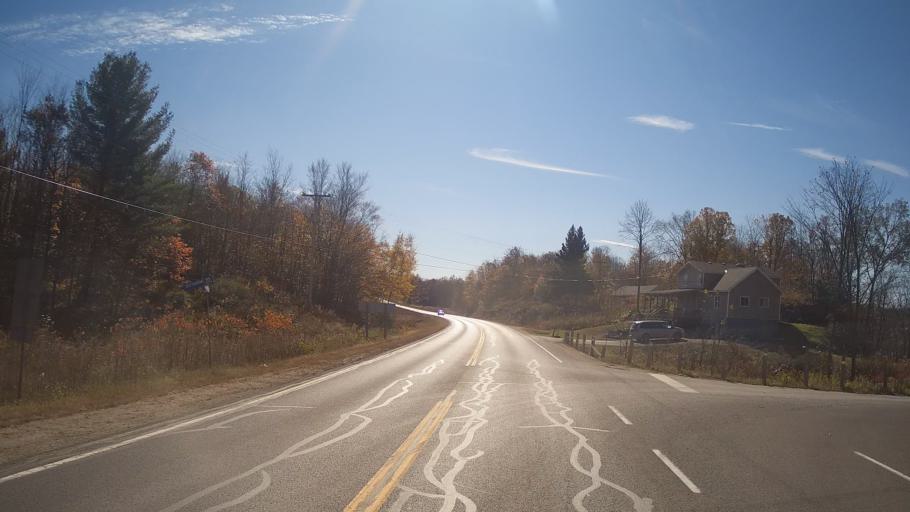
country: CA
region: Ontario
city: Perth
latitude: 44.7050
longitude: -76.6737
